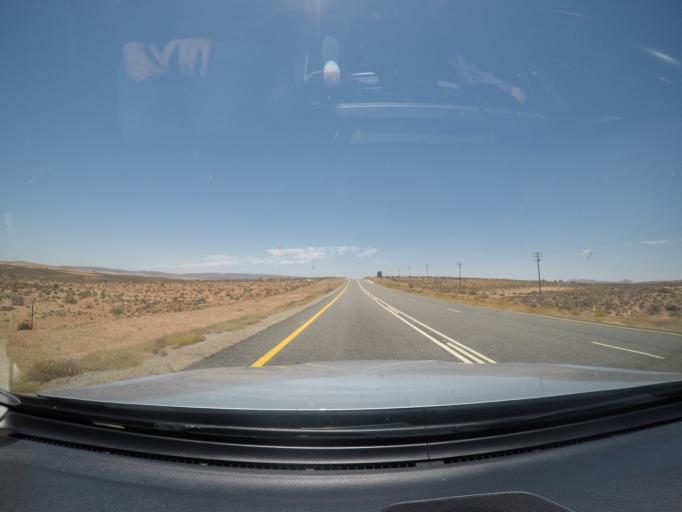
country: ZA
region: Northern Cape
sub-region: Namakwa District Municipality
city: Springbok
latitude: -29.3787
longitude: 17.7977
